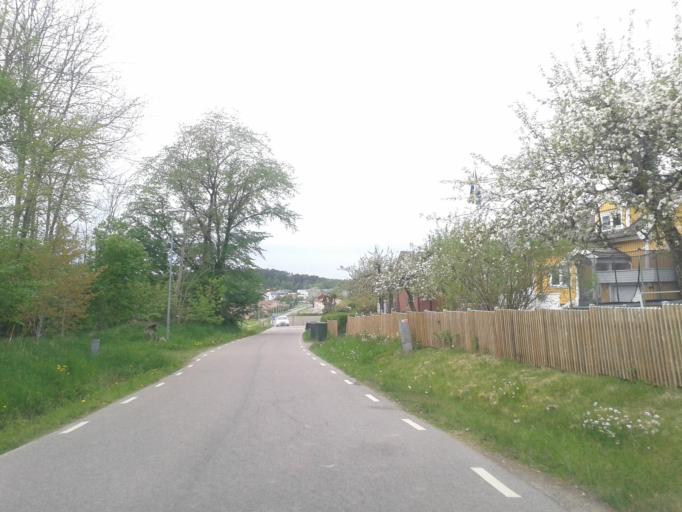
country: SE
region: Vaestra Goetaland
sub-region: Kungalvs Kommun
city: Kungalv
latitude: 57.8575
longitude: 11.9314
